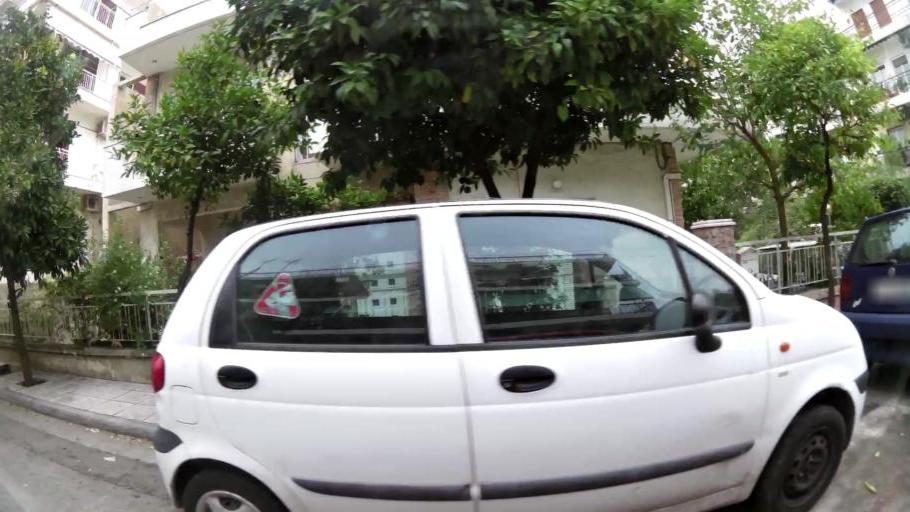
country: GR
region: Attica
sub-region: Nomarchia Athinas
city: Agioi Anargyroi
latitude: 38.0289
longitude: 23.7117
